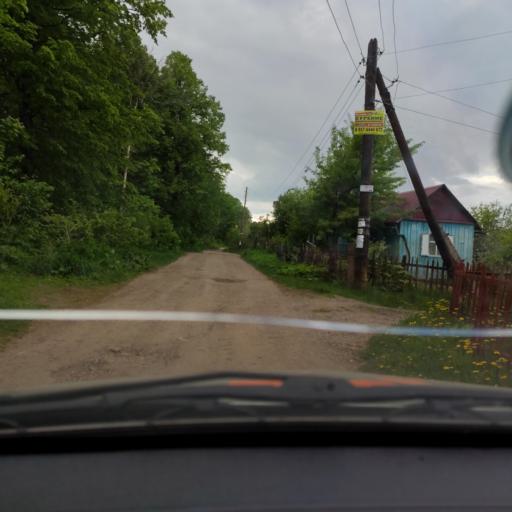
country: RU
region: Bashkortostan
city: Blagoveshchensk
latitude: 54.9400
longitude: 56.0886
